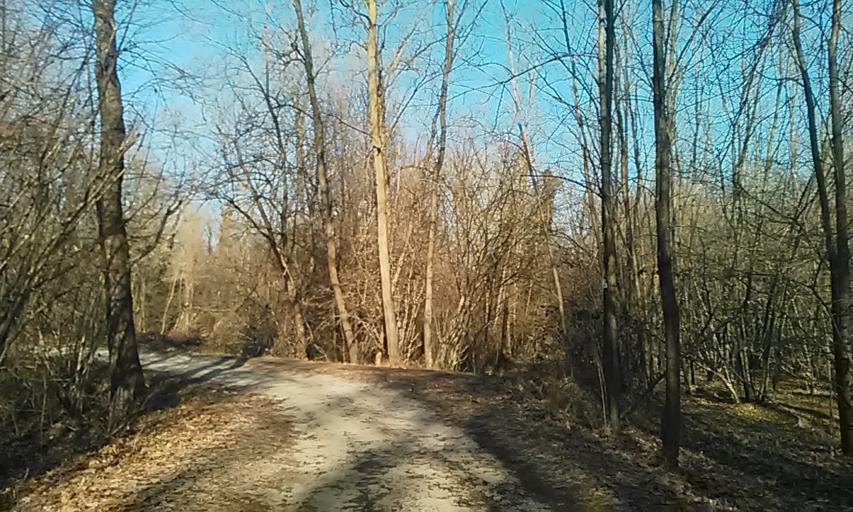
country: IT
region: Piedmont
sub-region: Provincia di Vercelli
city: Lenta
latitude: 45.5835
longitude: 8.3825
